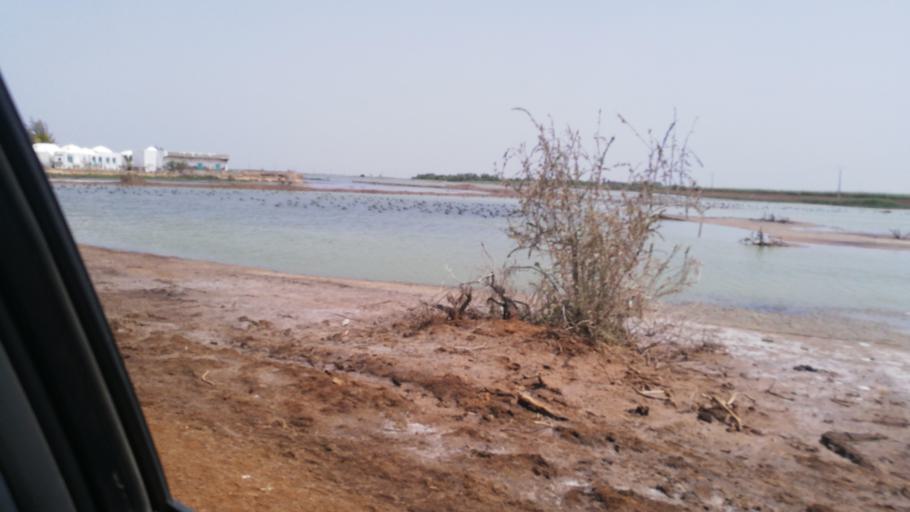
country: SN
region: Saint-Louis
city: Saint-Louis
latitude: 16.3611
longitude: -16.2761
